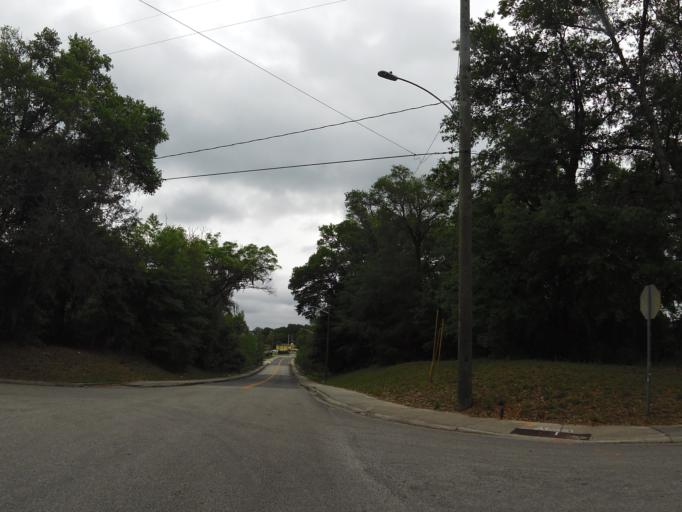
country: US
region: Florida
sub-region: Duval County
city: Jacksonville
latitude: 30.3229
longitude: -81.5664
